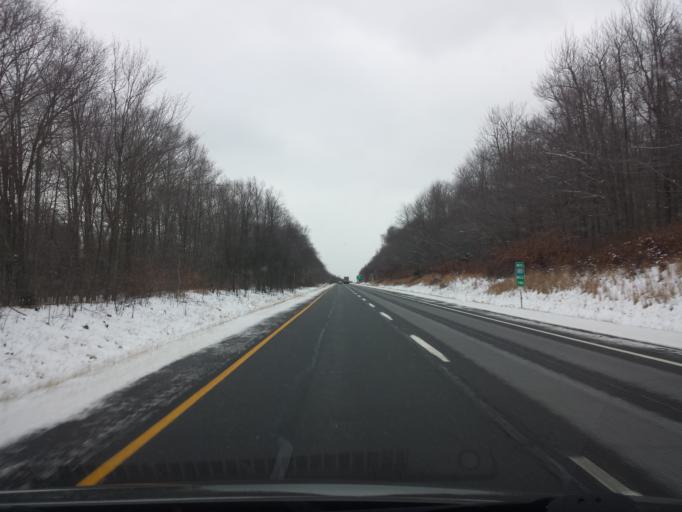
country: US
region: Pennsylvania
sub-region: Carbon County
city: Indian Mountain Lake
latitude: 41.0782
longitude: -75.5290
